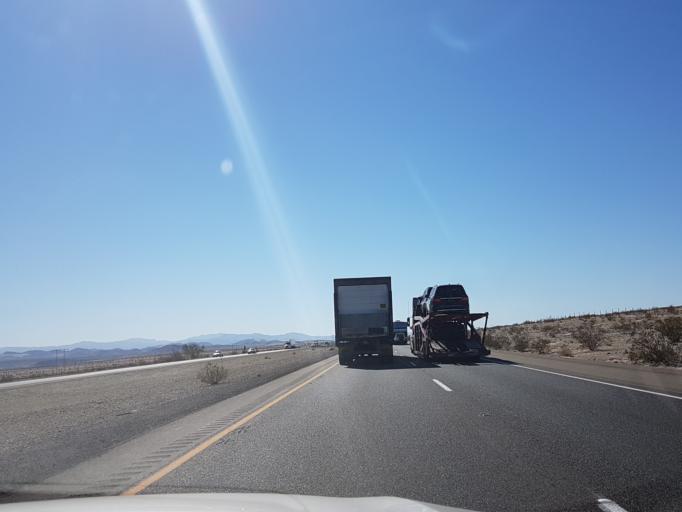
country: US
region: California
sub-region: San Bernardino County
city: Fort Irwin
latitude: 35.0460
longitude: -116.4509
